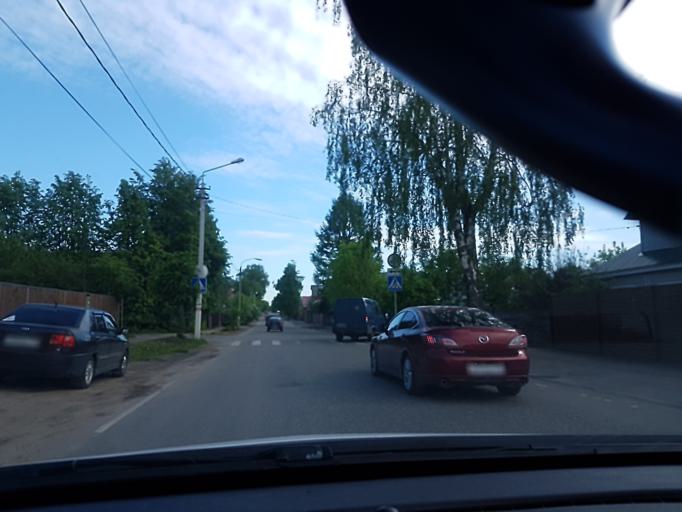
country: RU
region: Moskovskaya
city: Istra
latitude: 55.9170
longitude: 36.8681
